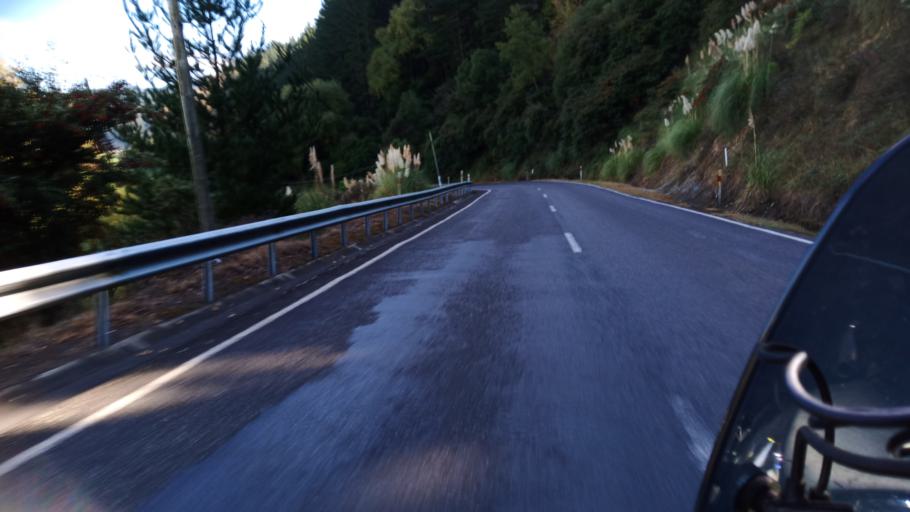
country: NZ
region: Hawke's Bay
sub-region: Wairoa District
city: Wairoa
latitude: -38.9260
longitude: 177.2739
